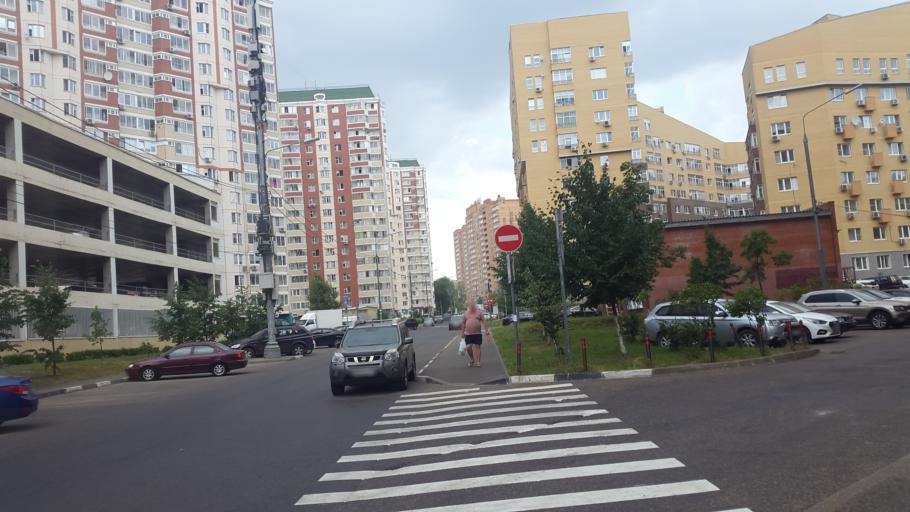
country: RU
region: Moskovskaya
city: Kommunarka
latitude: 55.5670
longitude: 37.4724
